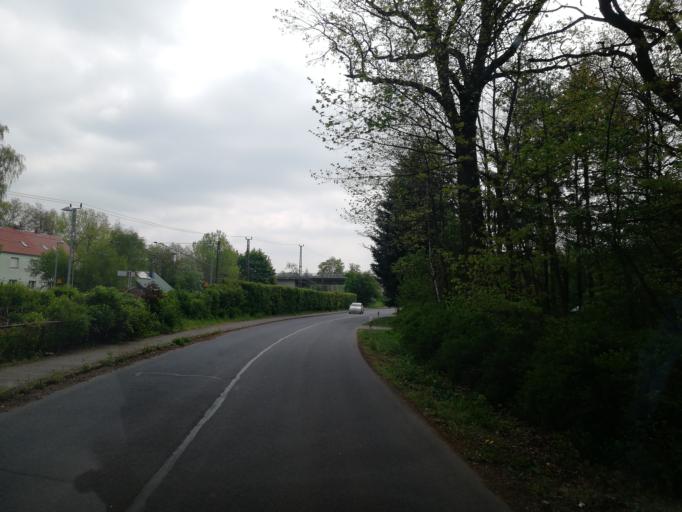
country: DE
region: Brandenburg
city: Herzberg
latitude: 51.6425
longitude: 13.1741
